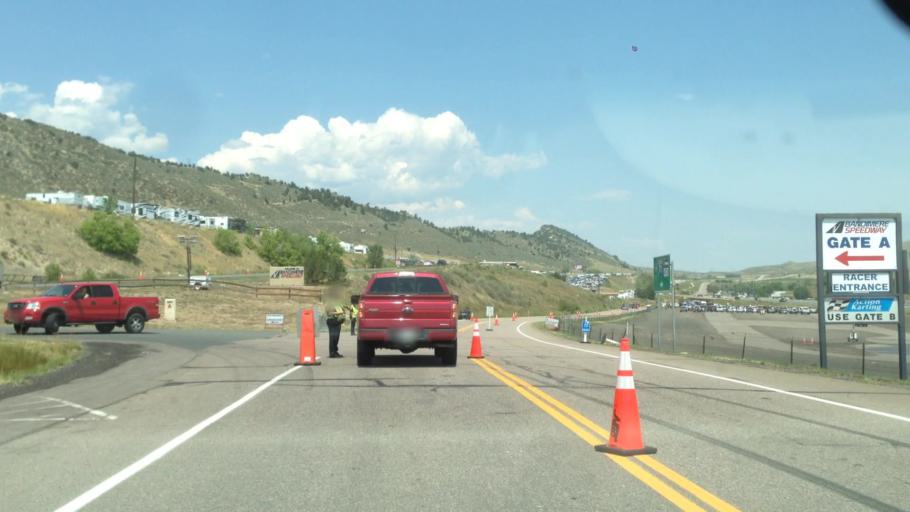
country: US
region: Colorado
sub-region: Jefferson County
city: Indian Hills
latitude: 39.6561
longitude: -105.1830
